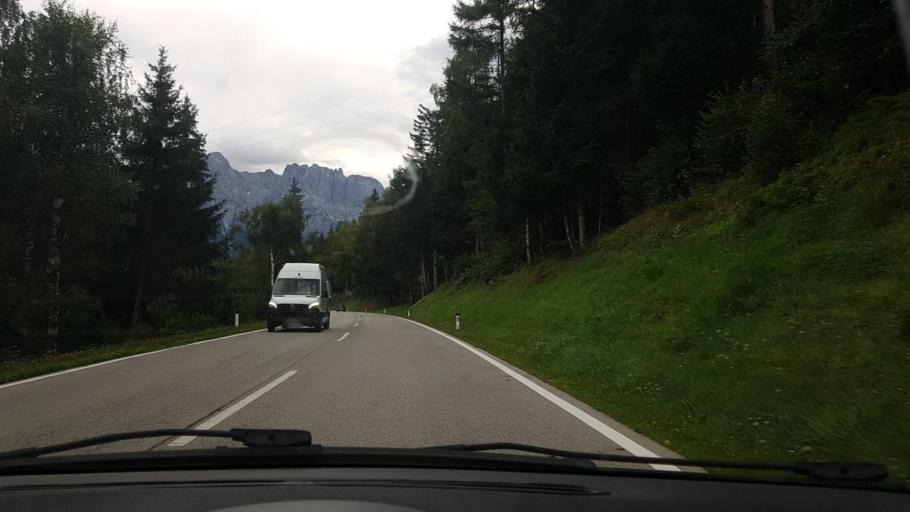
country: AT
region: Tyrol
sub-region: Politischer Bezirk Lienz
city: Dolsach
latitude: 46.8495
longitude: 12.8537
